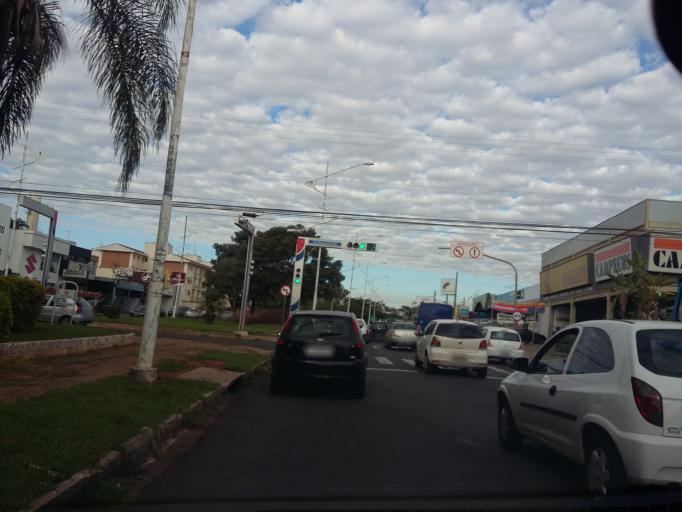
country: BR
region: Sao Paulo
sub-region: Sao Jose Do Rio Preto
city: Sao Jose do Rio Preto
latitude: -20.8213
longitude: -49.3992
